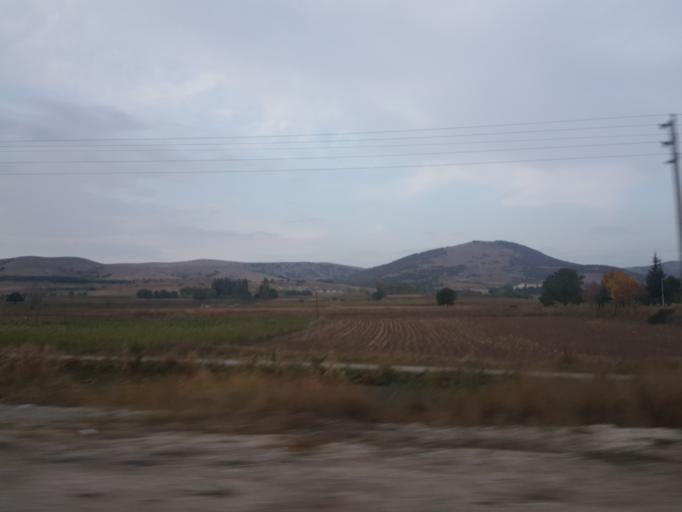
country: TR
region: Amasya
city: Gumushacikoy
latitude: 40.8866
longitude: 35.2069
